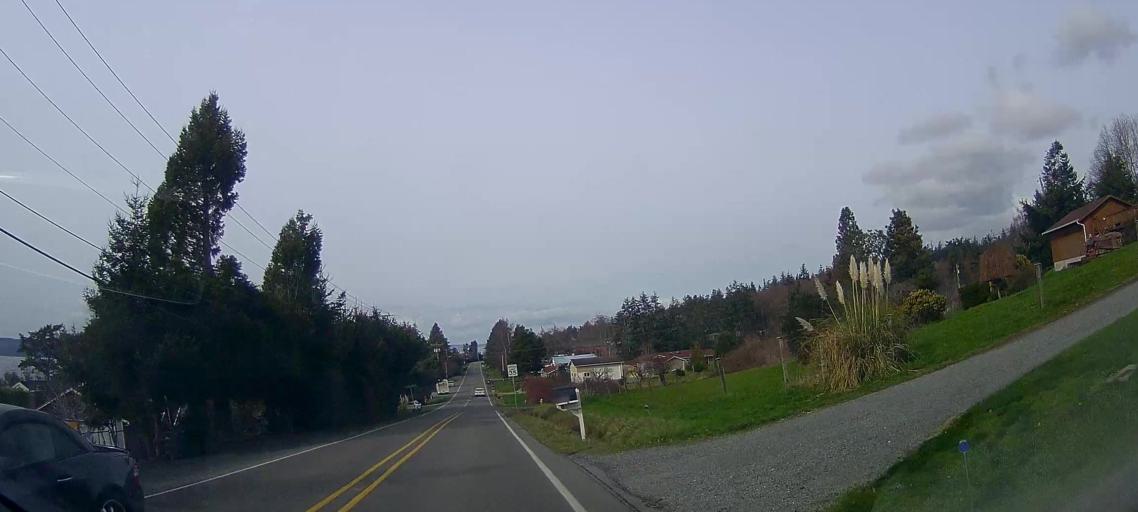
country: US
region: Washington
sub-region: Island County
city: Camano
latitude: 48.1681
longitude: -122.5243
